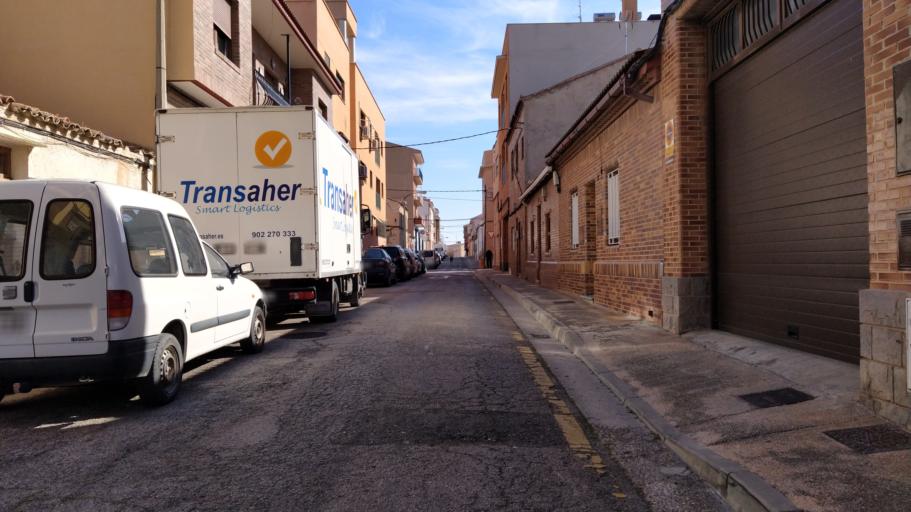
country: ES
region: Aragon
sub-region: Provincia de Zaragoza
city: Oliver-Valdefierro, Oliver, Valdefierro
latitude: 41.6385
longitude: -0.9362
